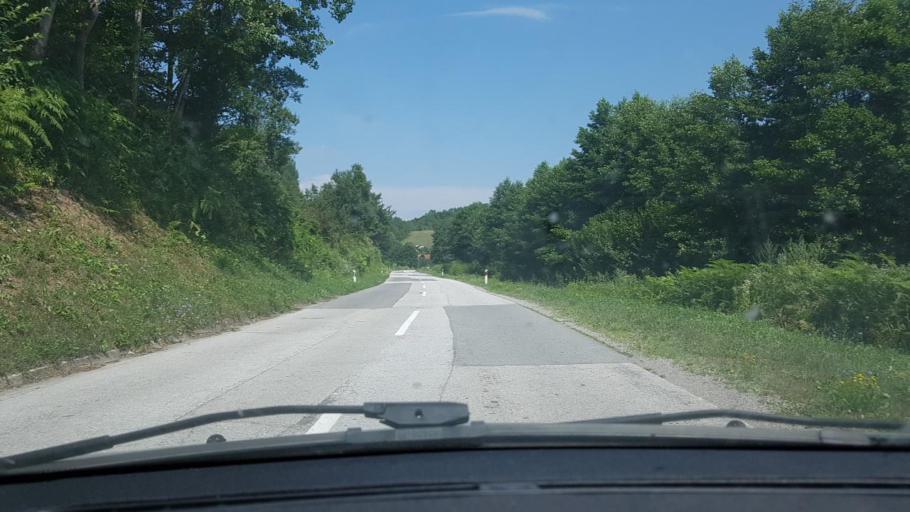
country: HR
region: Karlovacka
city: Vojnic
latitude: 45.2496
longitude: 15.7000
